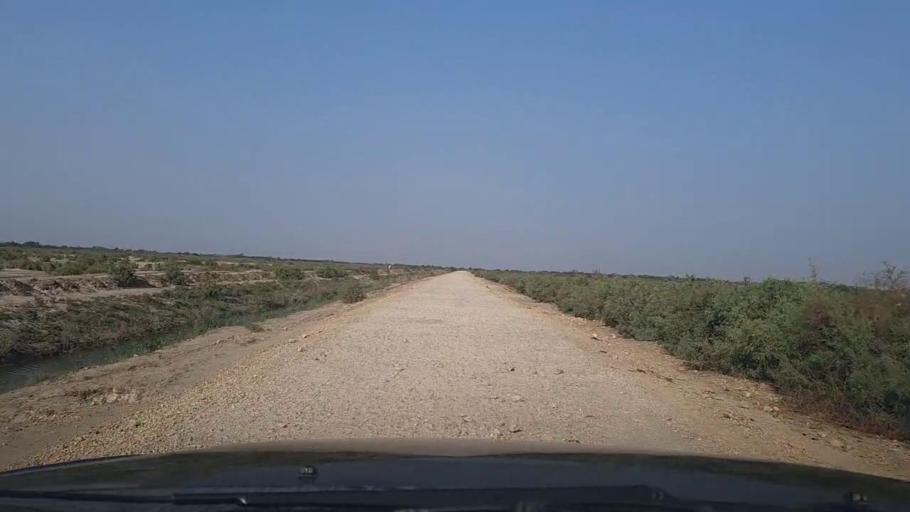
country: PK
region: Sindh
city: Mirpur Sakro
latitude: 24.6455
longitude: 67.7536
